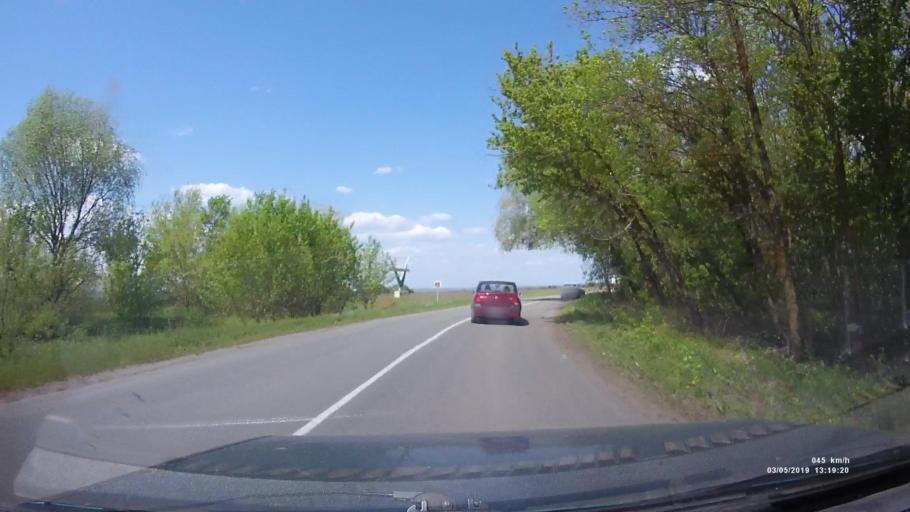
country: RU
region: Rostov
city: Semikarakorsk
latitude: 47.5369
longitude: 40.7477
